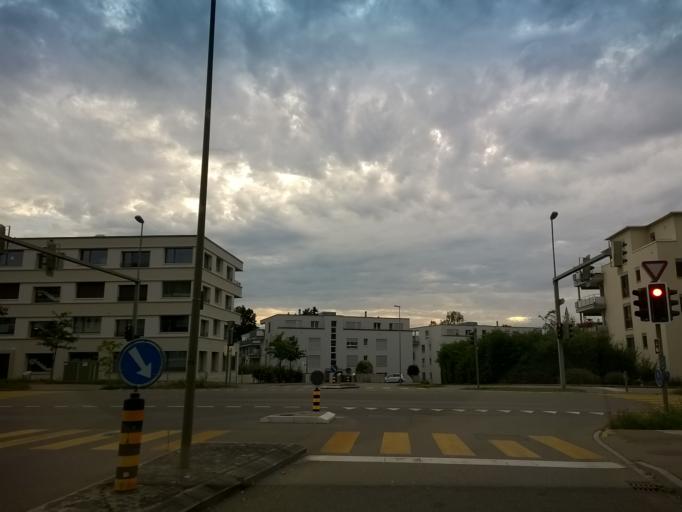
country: CH
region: Zurich
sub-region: Bezirk Buelach
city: Bachenbulach
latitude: 47.5101
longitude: 8.5445
